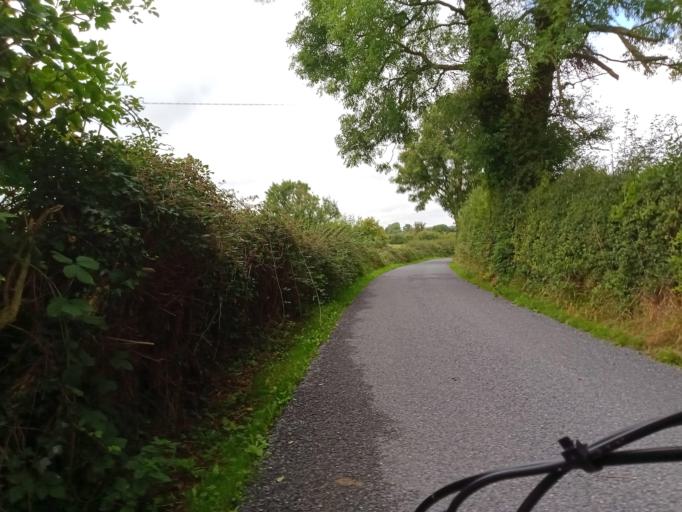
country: IE
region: Leinster
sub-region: Kilkenny
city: Callan
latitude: 52.5298
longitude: -7.2863
